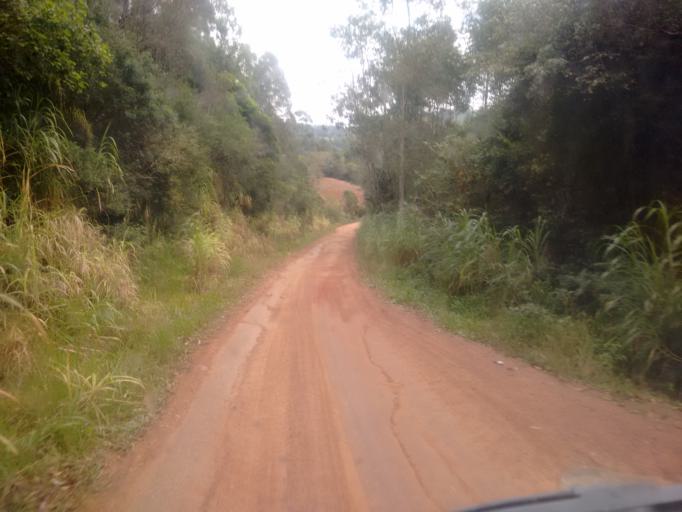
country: BR
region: Rio Grande do Sul
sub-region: Camaqua
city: Camaqua
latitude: -30.7230
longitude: -51.8618
